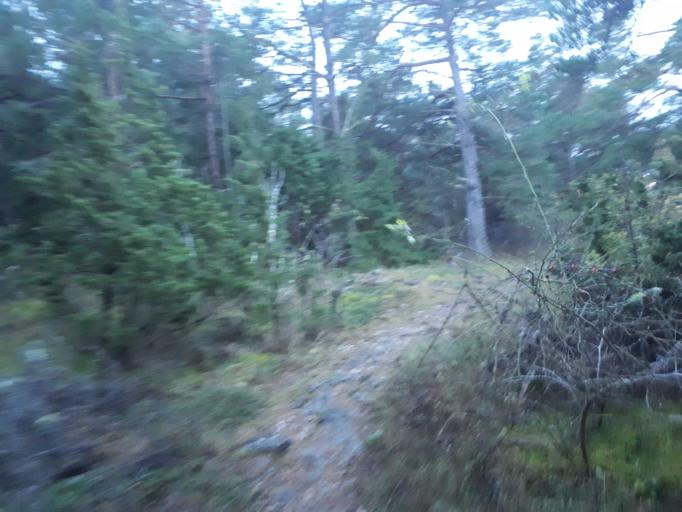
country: SE
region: Gotland
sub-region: Gotland
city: Visby
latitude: 57.6841
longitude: 18.3476
